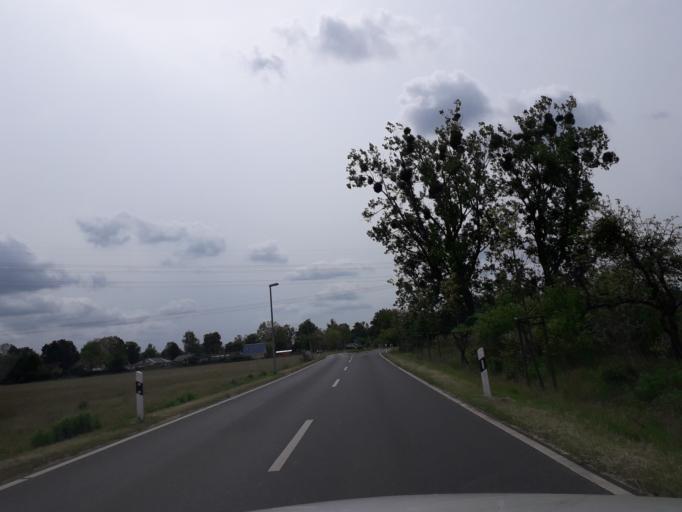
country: DE
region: Brandenburg
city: Brieselang
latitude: 52.6073
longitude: 12.9888
